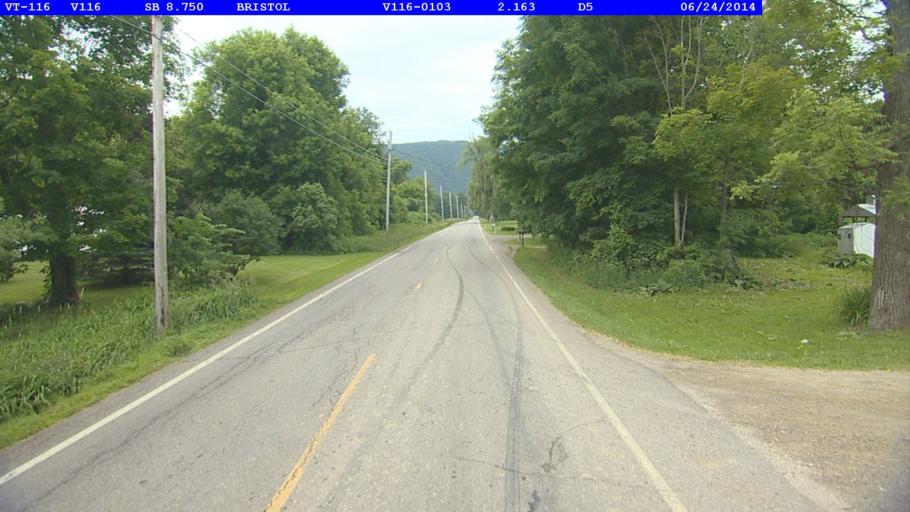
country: US
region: Vermont
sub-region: Addison County
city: Bristol
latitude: 44.0845
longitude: -73.0889
